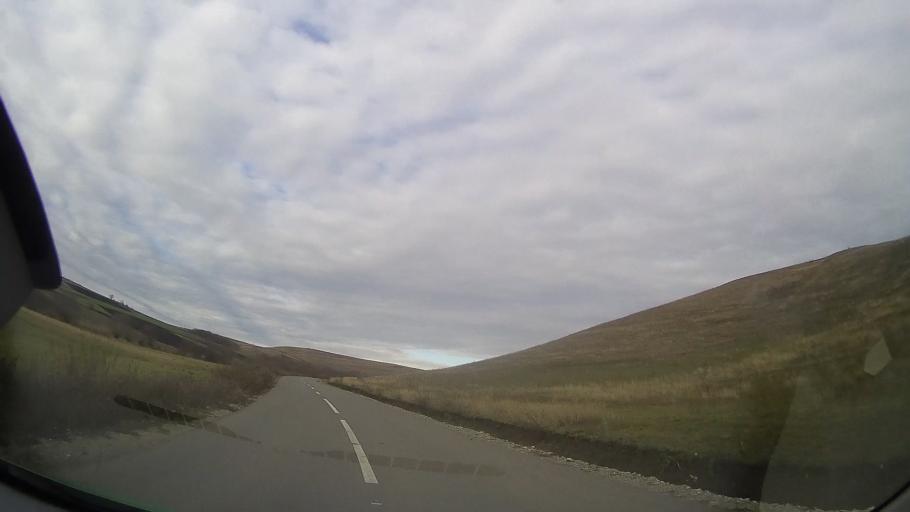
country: RO
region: Bistrita-Nasaud
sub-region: Comuna Silvasu de Campie
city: Silvasu de Campie
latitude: 46.8047
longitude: 24.2988
